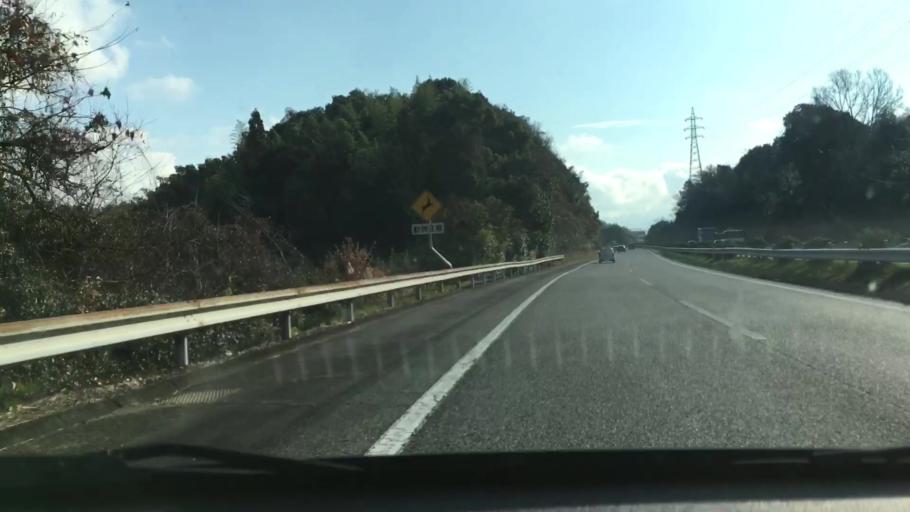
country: JP
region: Kumamoto
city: Matsubase
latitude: 32.6343
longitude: 130.7102
